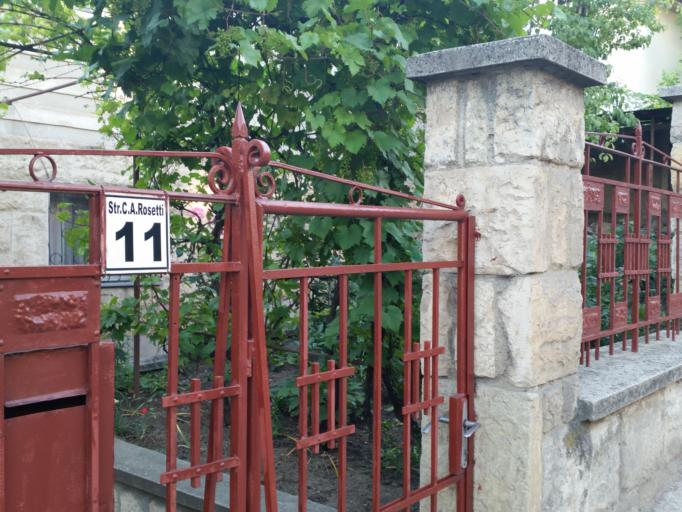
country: RO
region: Cluj
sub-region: Municipiul Cluj-Napoca
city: Cluj-Napoca
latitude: 46.7740
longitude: 23.5707
